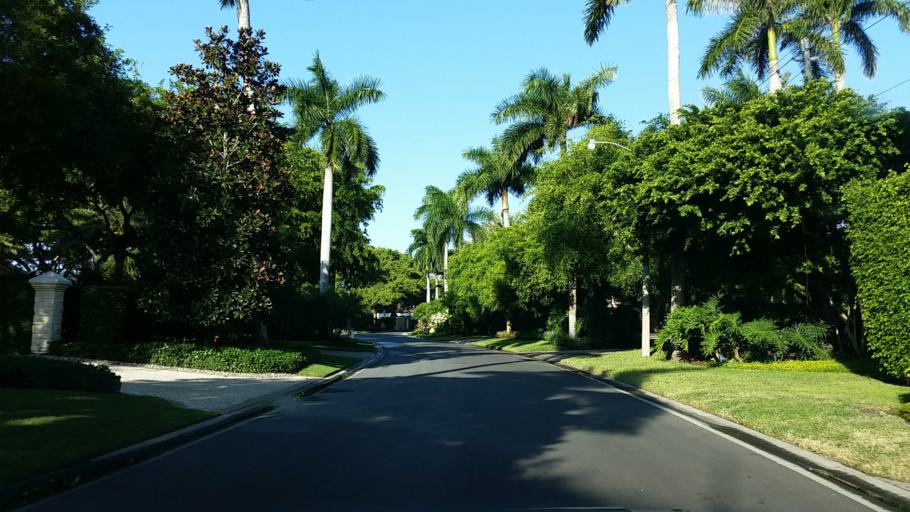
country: US
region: Florida
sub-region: Collier County
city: Naples
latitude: 26.1002
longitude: -81.7945
